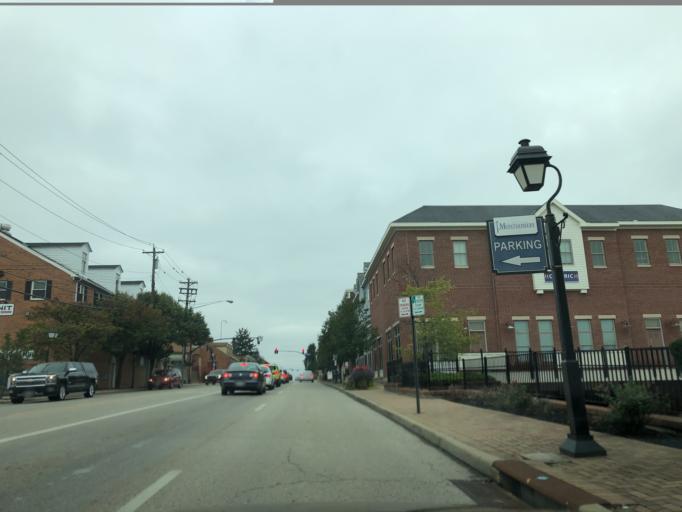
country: US
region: Ohio
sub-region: Hamilton County
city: Montgomery
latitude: 39.2256
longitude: -84.3553
